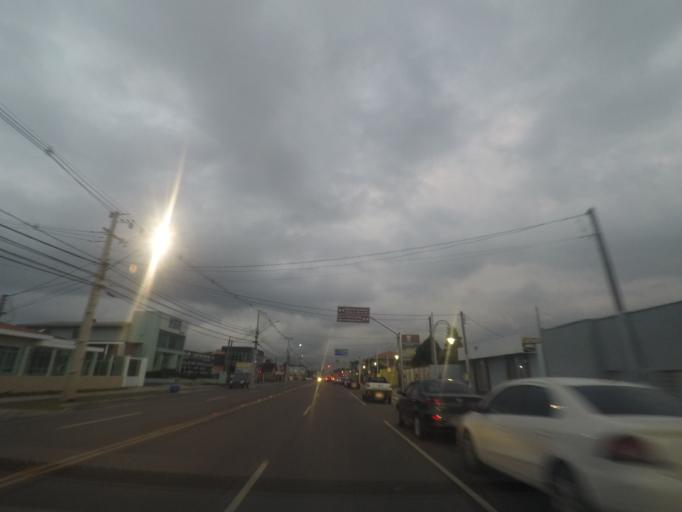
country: BR
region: Parana
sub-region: Curitiba
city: Curitiba
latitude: -25.4001
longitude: -49.3362
